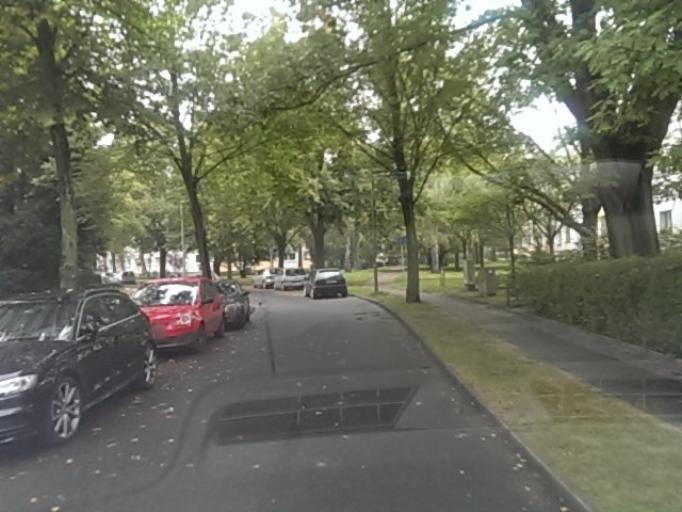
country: DE
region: Brandenburg
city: Teltow
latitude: 52.4123
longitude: 13.2551
